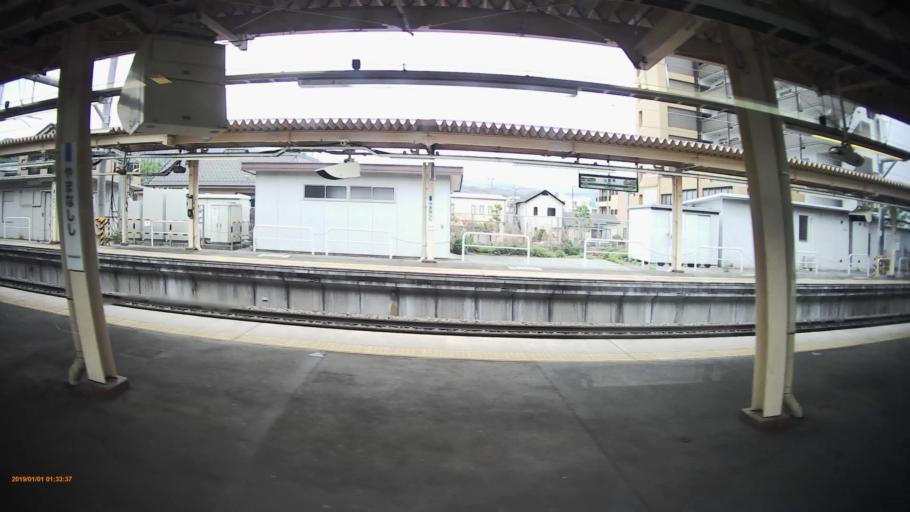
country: JP
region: Yamanashi
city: Enzan
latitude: 35.6851
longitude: 138.6826
